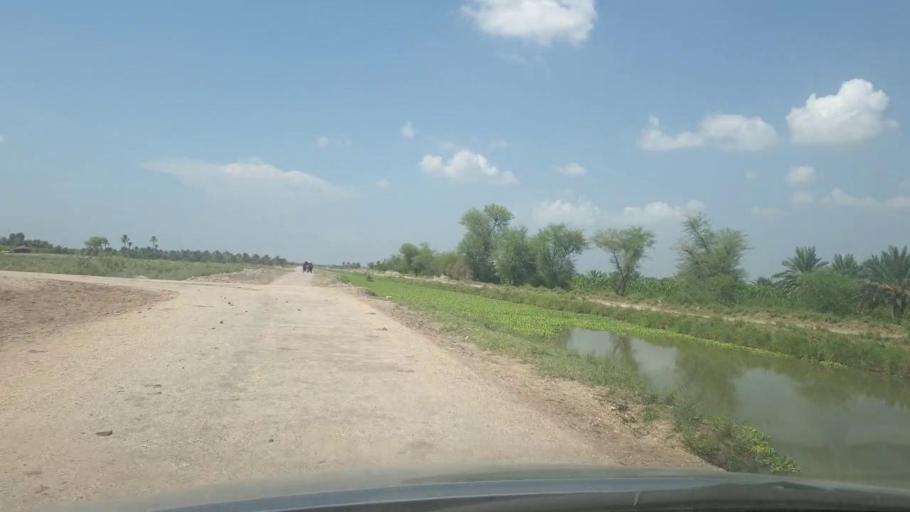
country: PK
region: Sindh
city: Khairpur
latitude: 27.5234
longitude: 68.8170
